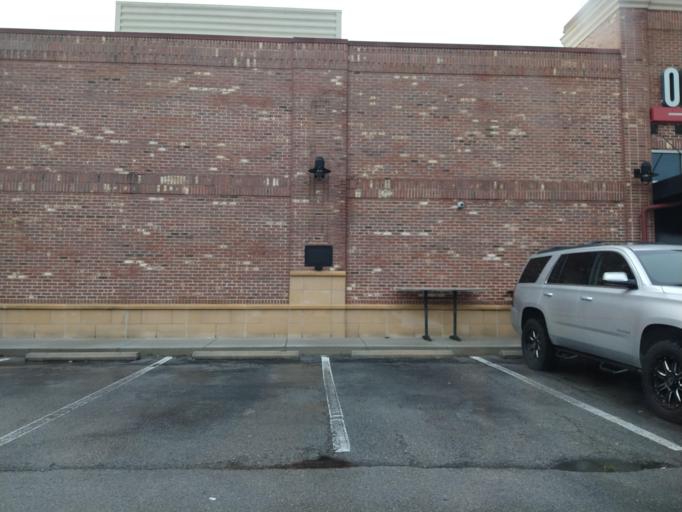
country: US
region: North Carolina
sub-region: Onslow County
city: Pumpkin Center
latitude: 34.7984
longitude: -77.4153
